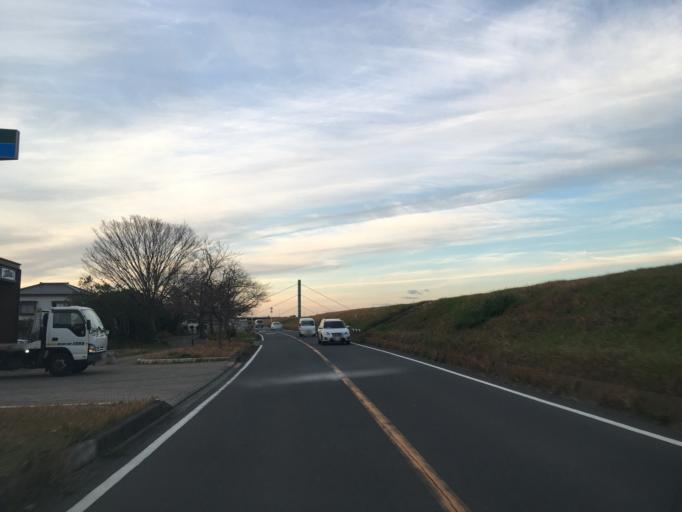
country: JP
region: Chiba
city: Katori-shi
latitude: 35.9040
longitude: 140.4972
